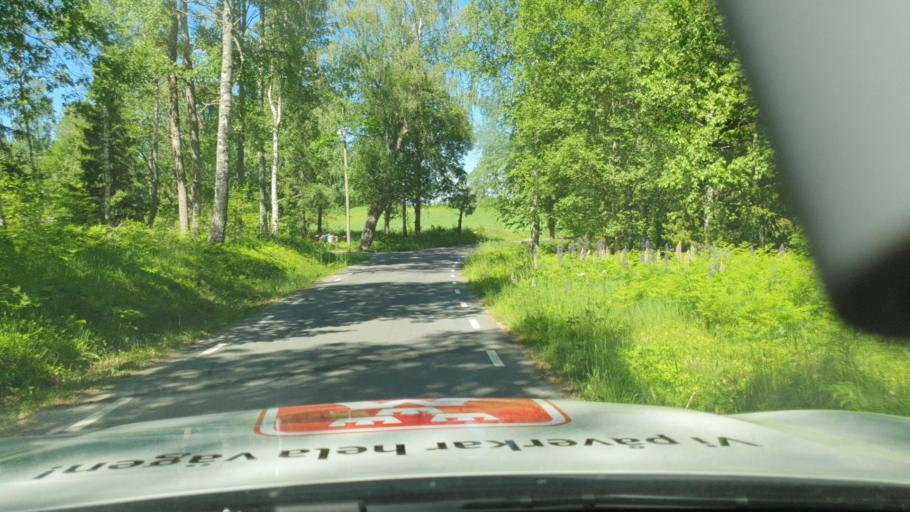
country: SE
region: Joenkoeping
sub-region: Habo Kommun
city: Habo
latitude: 57.9056
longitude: 14.0481
